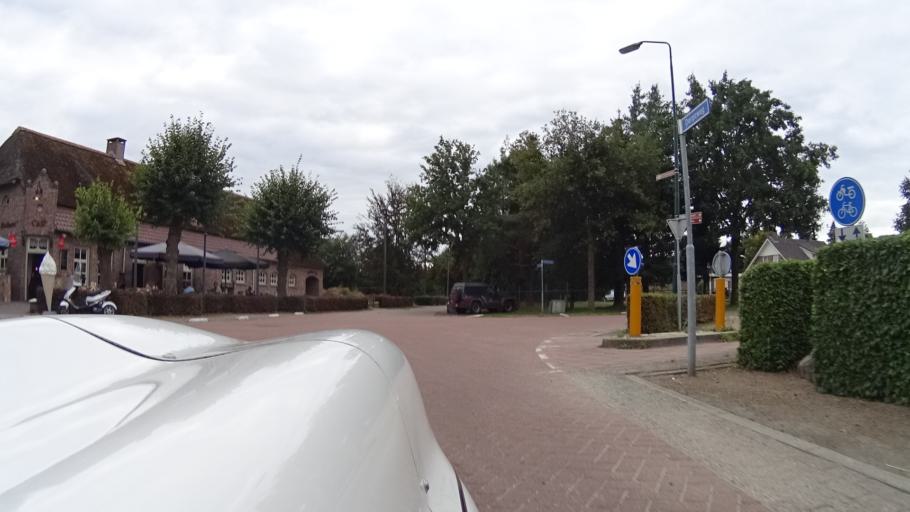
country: NL
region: North Brabant
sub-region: Gemeente Veghel
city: Mariaheide
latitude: 51.6578
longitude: 5.5627
